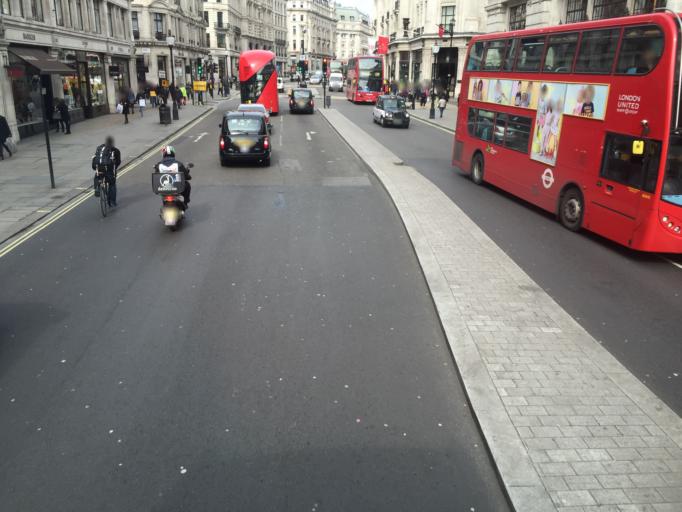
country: GB
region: England
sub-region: Greater London
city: London
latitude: 51.5132
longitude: -0.1409
